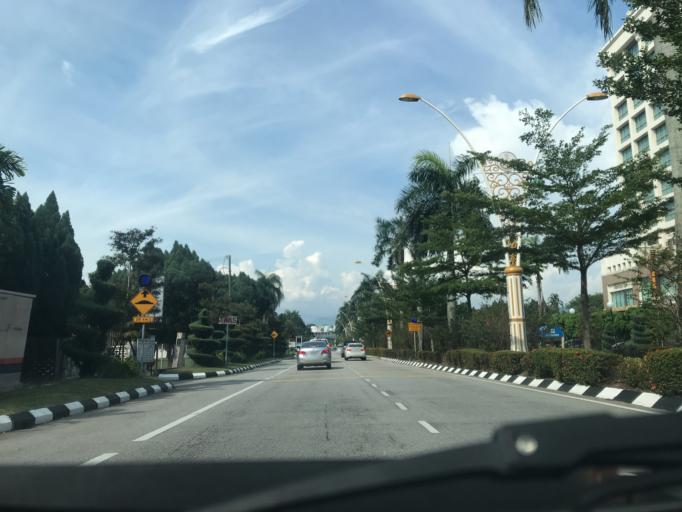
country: MY
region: Perak
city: Ipoh
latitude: 4.5955
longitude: 101.0994
